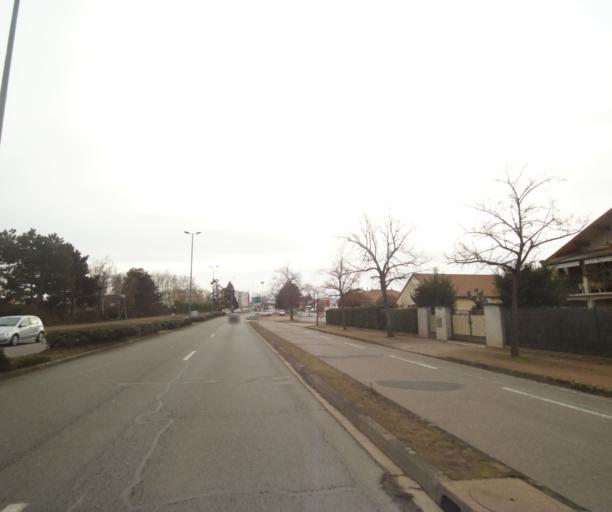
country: FR
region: Rhone-Alpes
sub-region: Departement de la Loire
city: Roanne
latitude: 46.0521
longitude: 4.0684
